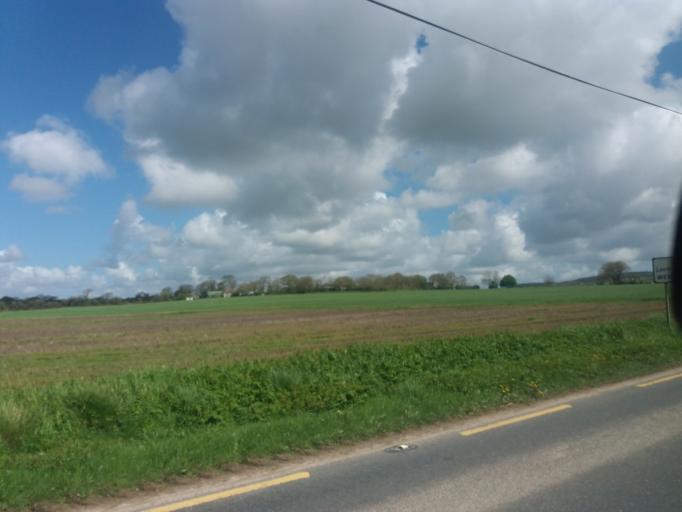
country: IE
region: Leinster
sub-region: Loch Garman
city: Loch Garman
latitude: 52.2853
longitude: -6.6274
